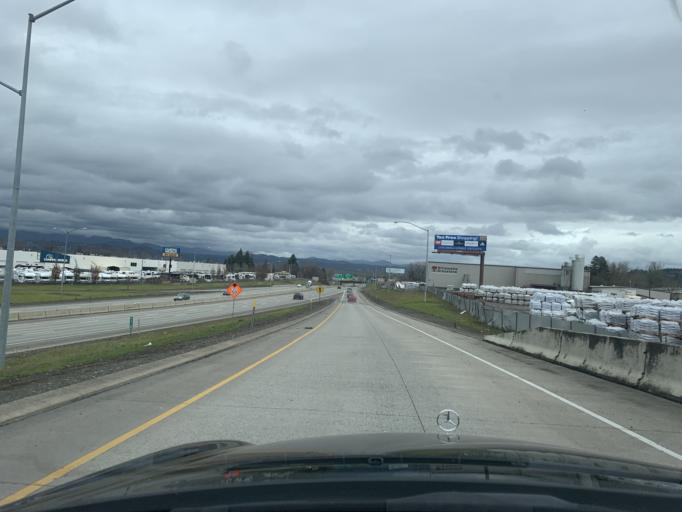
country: US
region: Oregon
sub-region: Multnomah County
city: Wood Village
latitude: 45.5398
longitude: -122.4169
